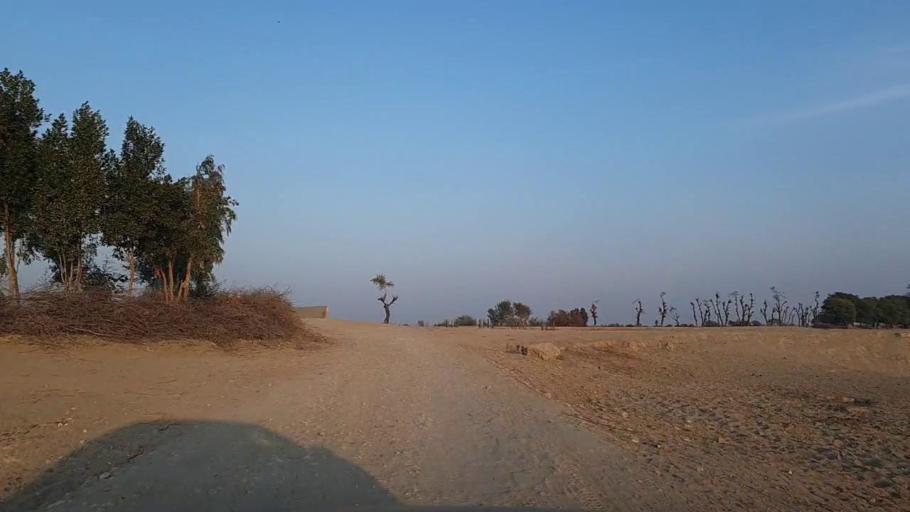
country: PK
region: Sindh
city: Sanghar
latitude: 25.9629
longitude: 69.0634
